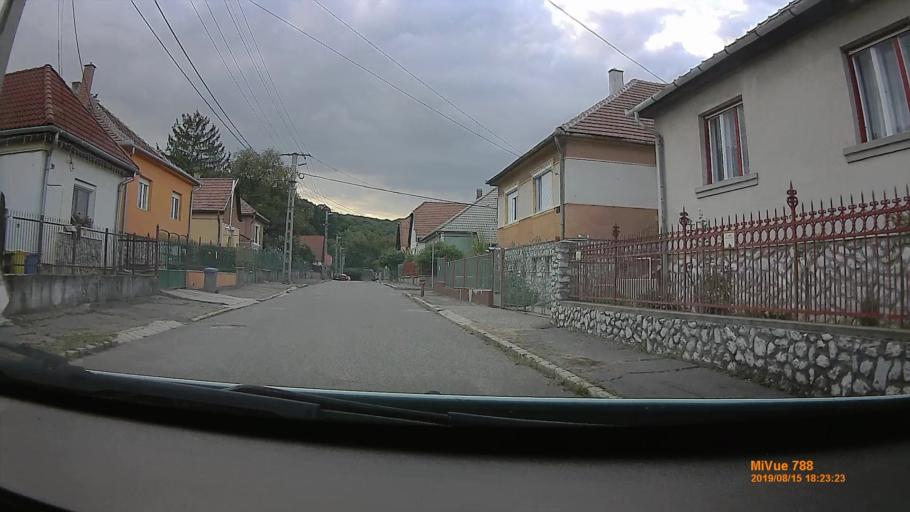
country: HU
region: Borsod-Abauj-Zemplen
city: Sajobabony
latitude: 48.1064
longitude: 20.6707
